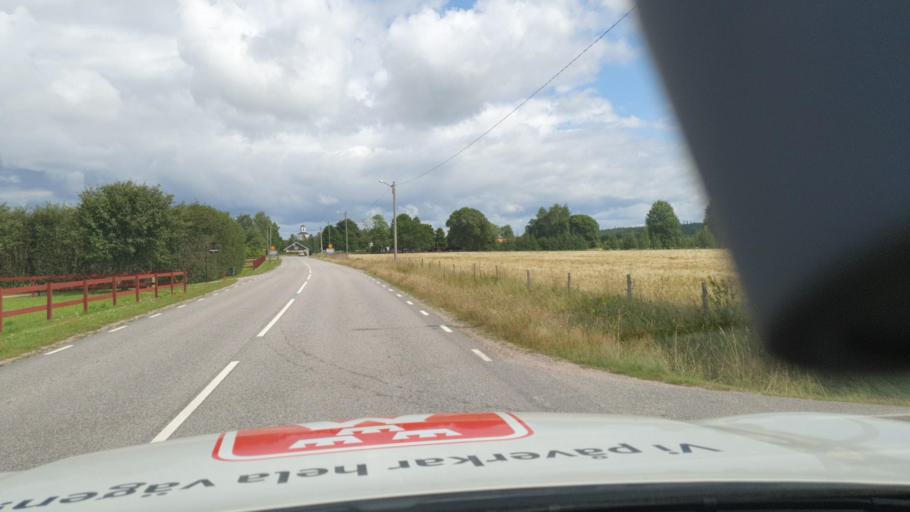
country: SE
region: Vaestra Goetaland
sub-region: Tranemo Kommun
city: Langhem
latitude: 57.5940
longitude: 13.2409
